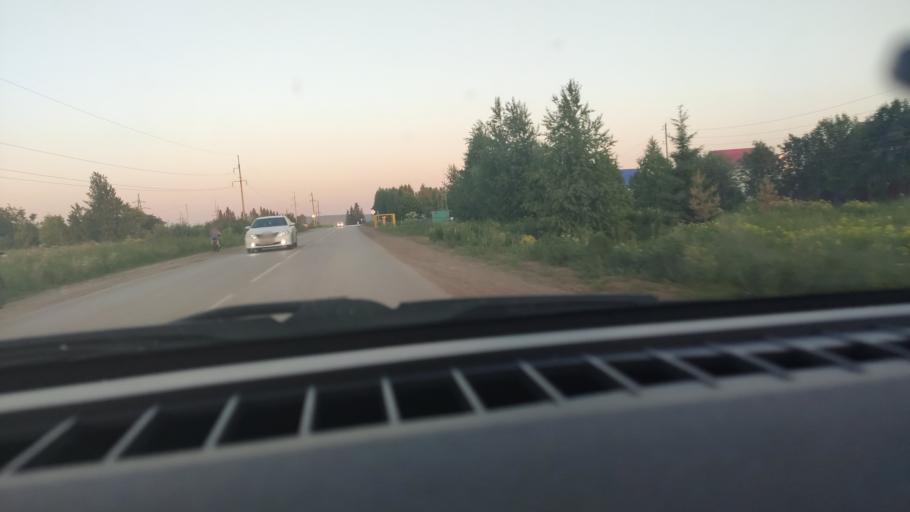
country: RU
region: Perm
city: Kultayevo
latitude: 57.8911
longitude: 55.9196
